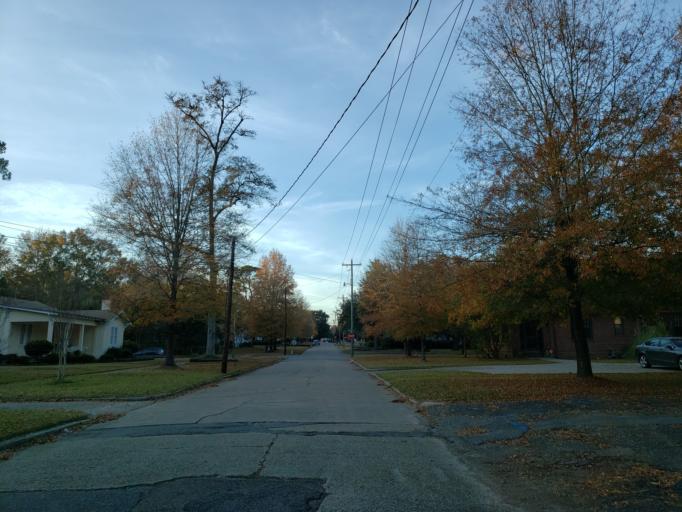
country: US
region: Mississippi
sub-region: Forrest County
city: Hattiesburg
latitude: 31.3223
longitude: -89.2968
